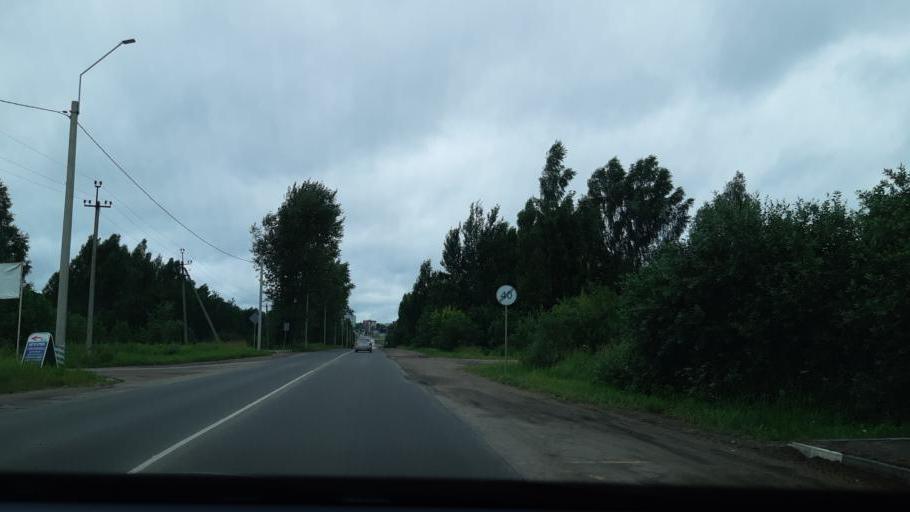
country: RU
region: Smolensk
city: Desnogorsk
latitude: 54.1360
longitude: 33.2776
